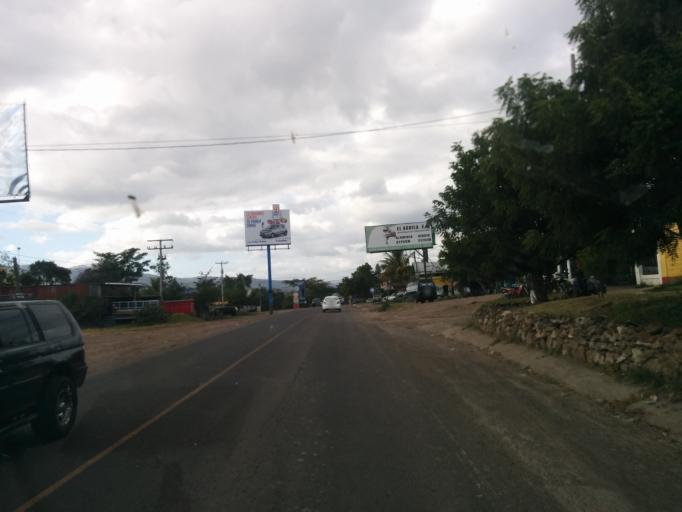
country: NI
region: Esteli
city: Esteli
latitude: 13.0632
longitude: -86.3463
